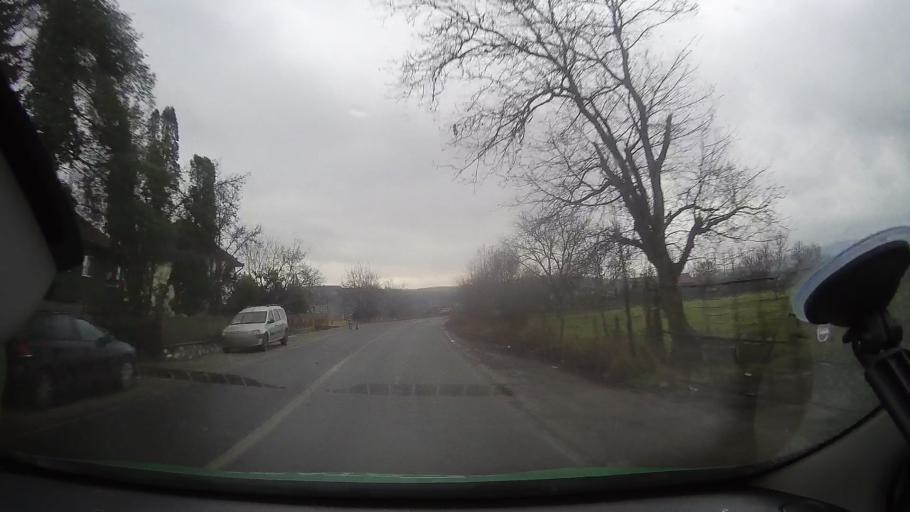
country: RO
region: Arad
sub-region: Comuna Halmagiu
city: Halmagiu
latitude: 46.2673
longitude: 22.5972
